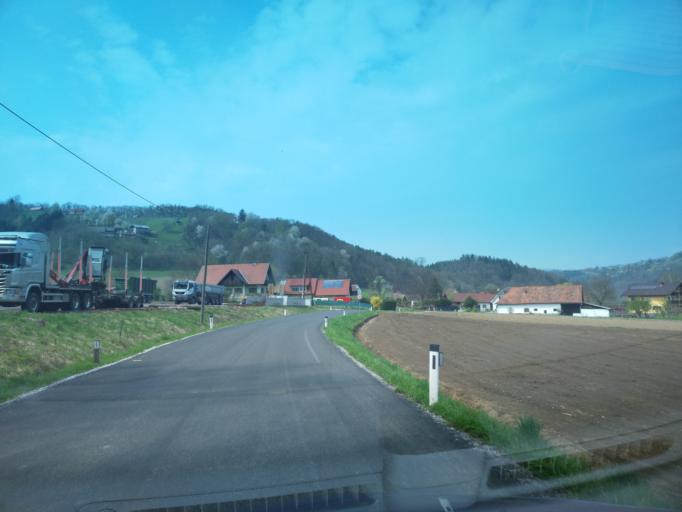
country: AT
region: Styria
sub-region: Politischer Bezirk Leibnitz
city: Kitzeck im Sausal
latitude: 46.7477
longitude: 15.4206
